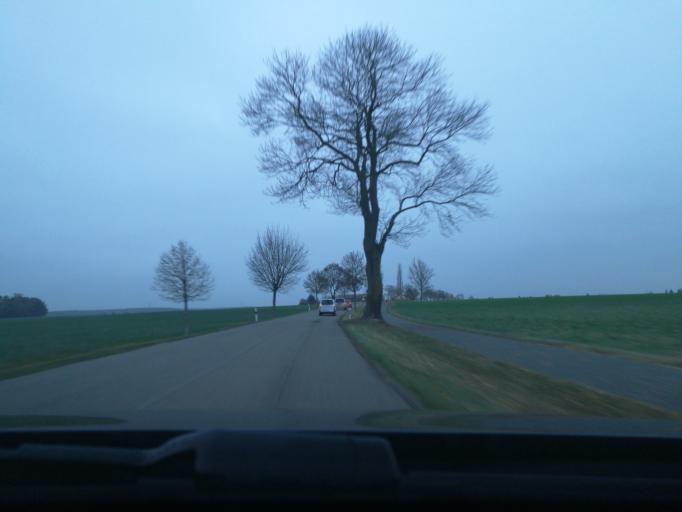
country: DE
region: Bavaria
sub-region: Regierungsbezirk Mittelfranken
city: Obermichelbach
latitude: 49.5202
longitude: 10.9159
